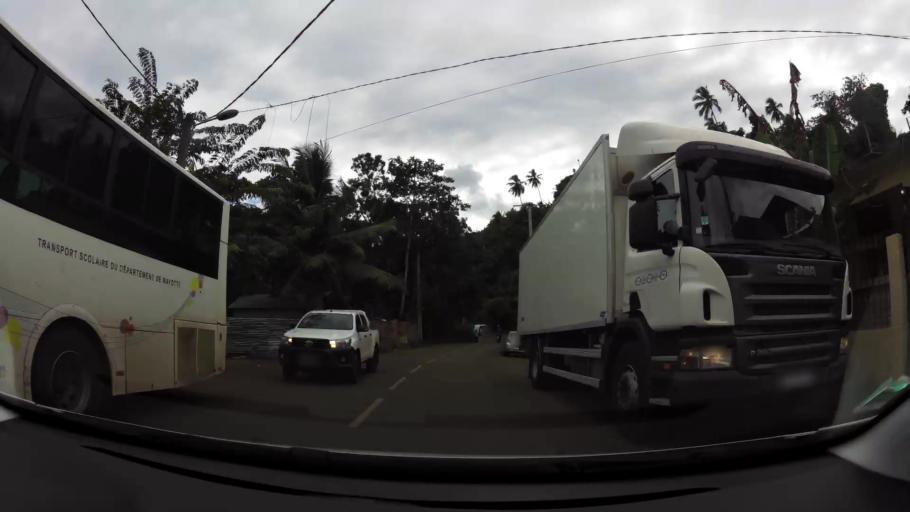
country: YT
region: Chiconi
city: Chiconi
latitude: -12.8400
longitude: 45.1214
